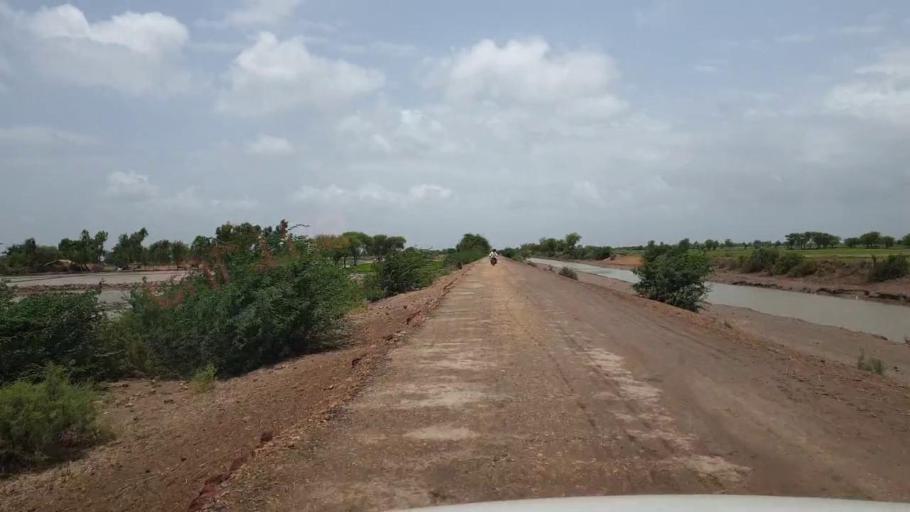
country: PK
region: Sindh
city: Kario
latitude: 24.7095
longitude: 68.6018
